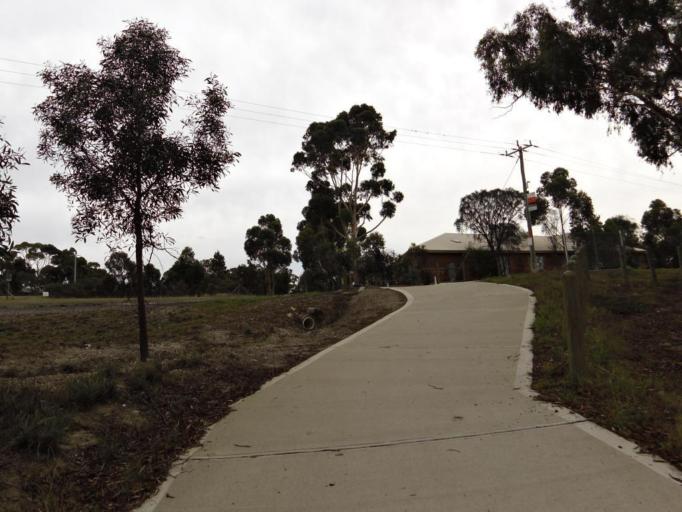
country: AU
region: Victoria
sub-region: Hume
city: Sunbury
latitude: -37.5626
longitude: 144.7157
